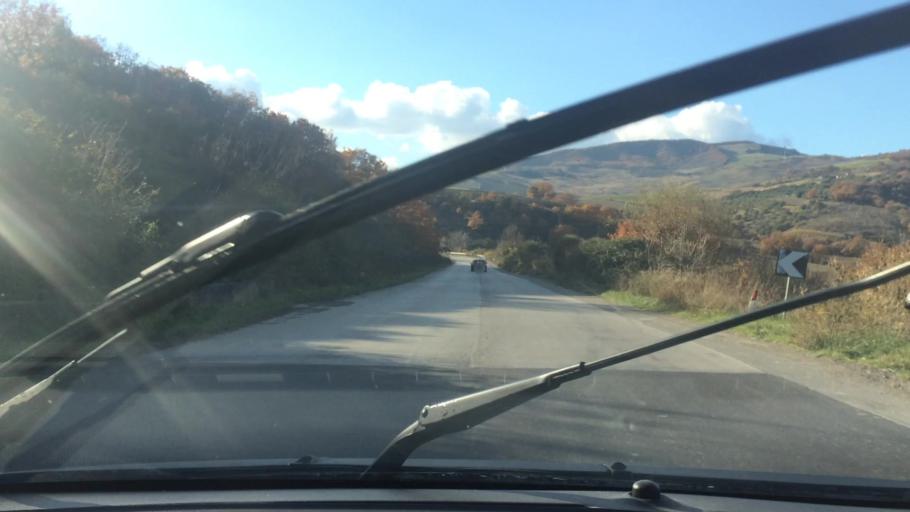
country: IT
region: Basilicate
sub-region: Provincia di Potenza
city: Tolve
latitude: 40.7224
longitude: 16.0397
